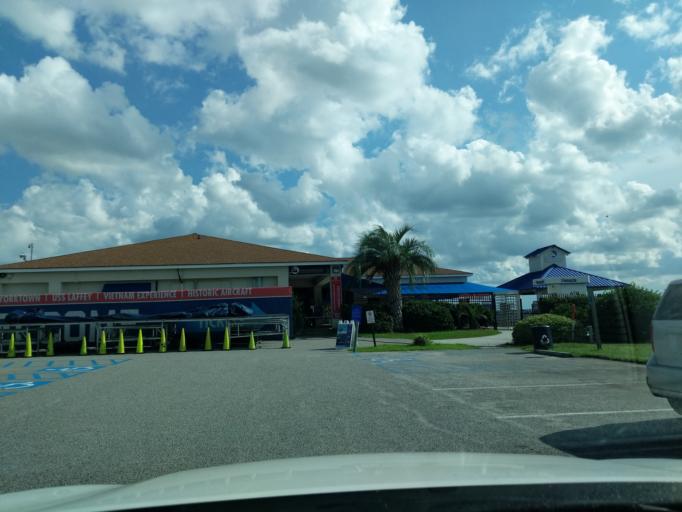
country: US
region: South Carolina
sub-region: Charleston County
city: Charleston
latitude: 32.7910
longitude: -79.9056
